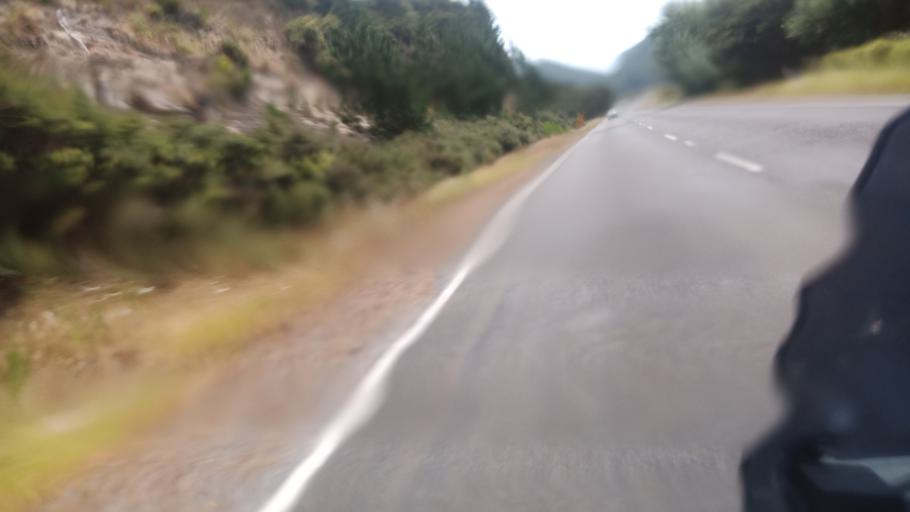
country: NZ
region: Bay of Plenty
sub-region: Opotiki District
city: Opotiki
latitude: -37.5716
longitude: 178.0102
